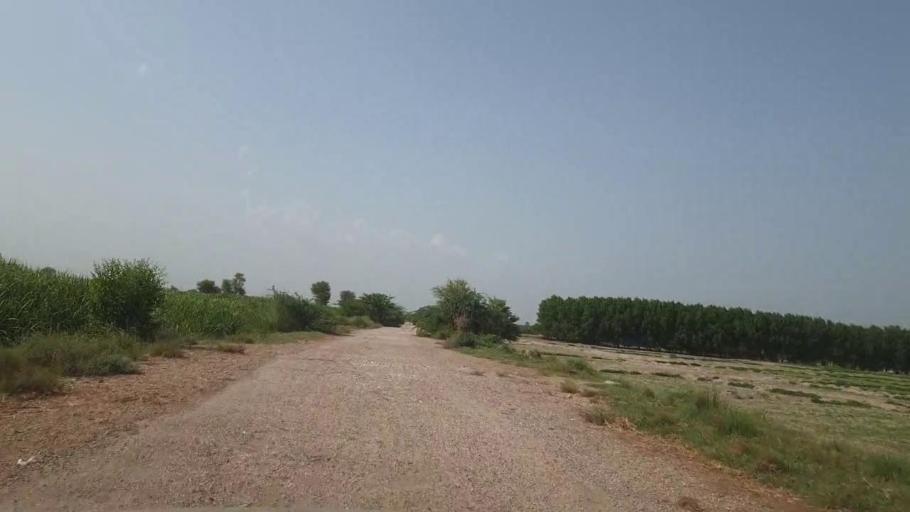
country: PK
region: Sindh
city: Pano Aqil
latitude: 27.7807
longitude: 69.1600
